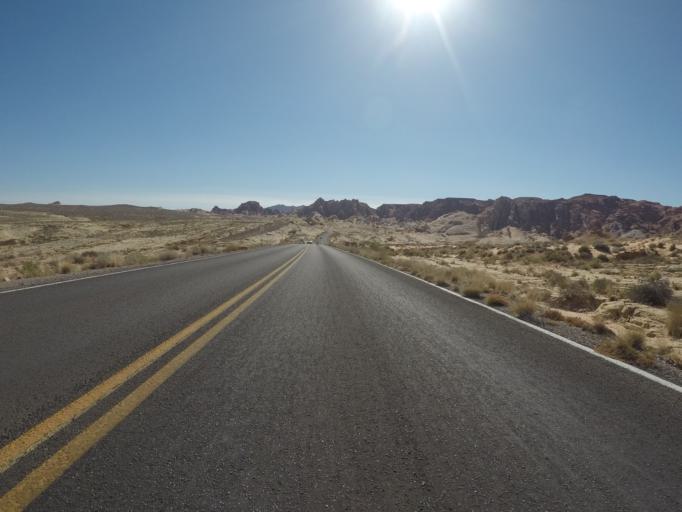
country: US
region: Nevada
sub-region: Clark County
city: Moapa Valley
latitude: 36.4689
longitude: -114.5252
